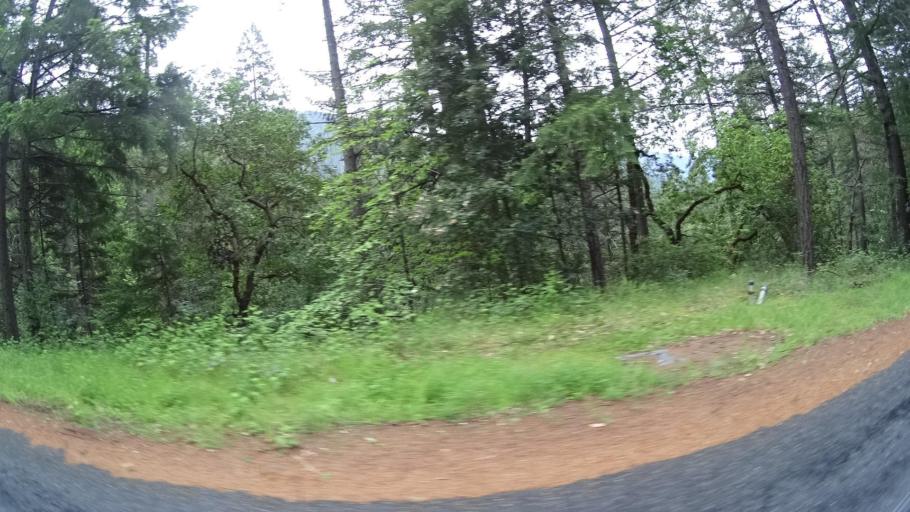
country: US
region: California
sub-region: Humboldt County
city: Willow Creek
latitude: 41.3414
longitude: -123.5129
